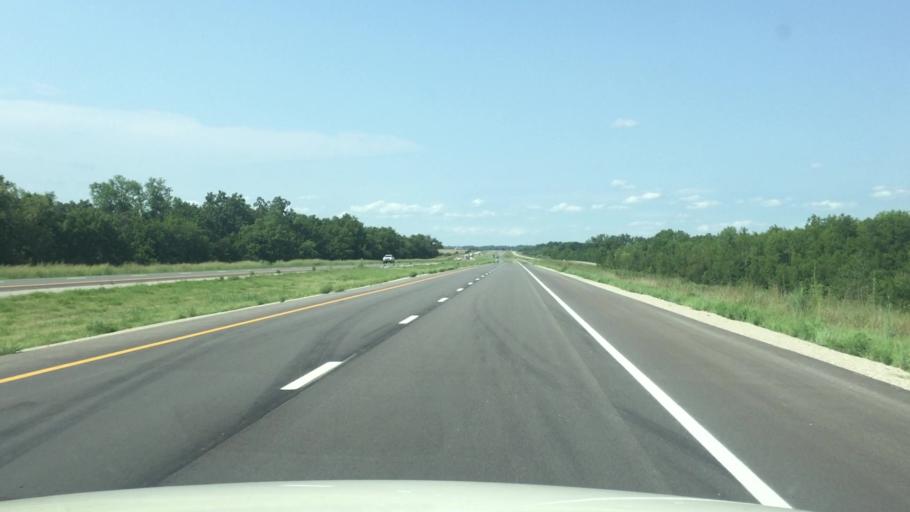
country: US
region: Kansas
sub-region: Linn County
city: La Cygne
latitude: 38.3014
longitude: -94.6773
